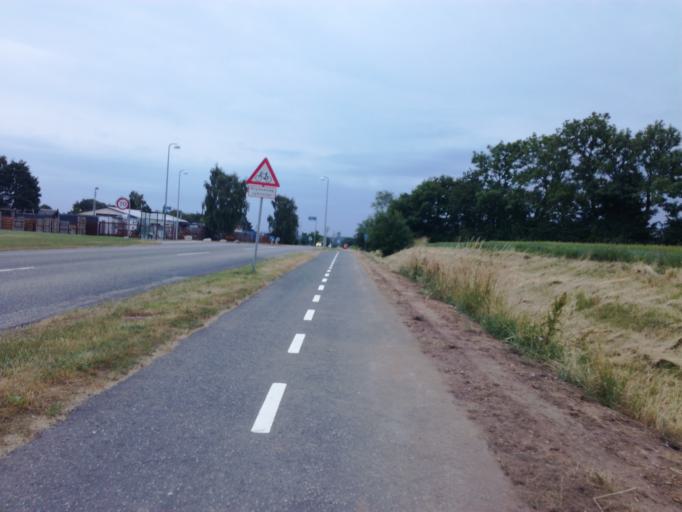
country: DK
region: South Denmark
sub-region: Vejle Kommune
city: Borkop
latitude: 55.6642
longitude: 9.6275
